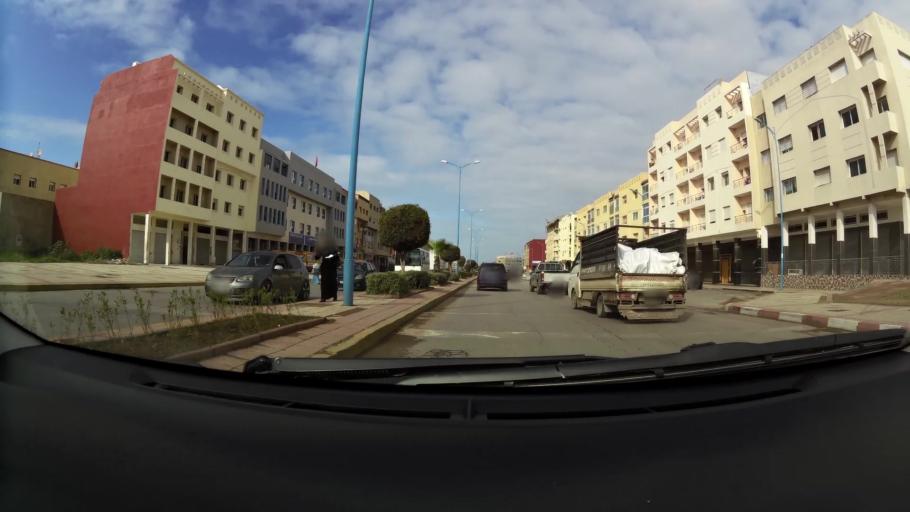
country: MA
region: Grand Casablanca
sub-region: Mohammedia
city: Mohammedia
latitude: 33.6969
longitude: -7.3668
